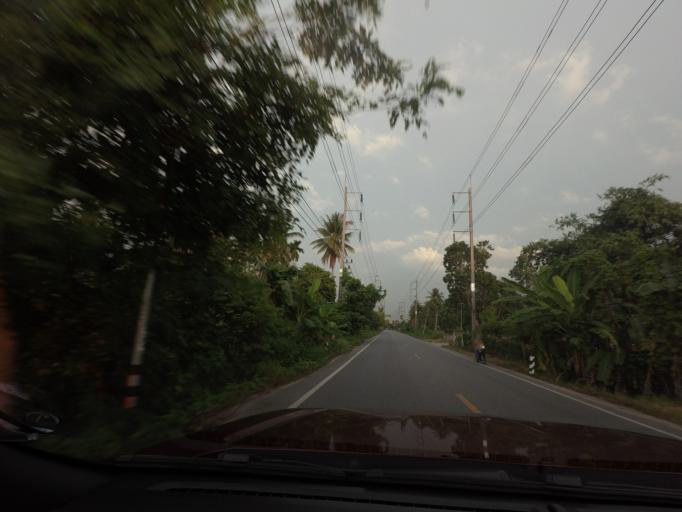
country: TH
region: Yala
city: Yala
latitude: 6.5720
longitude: 101.2028
